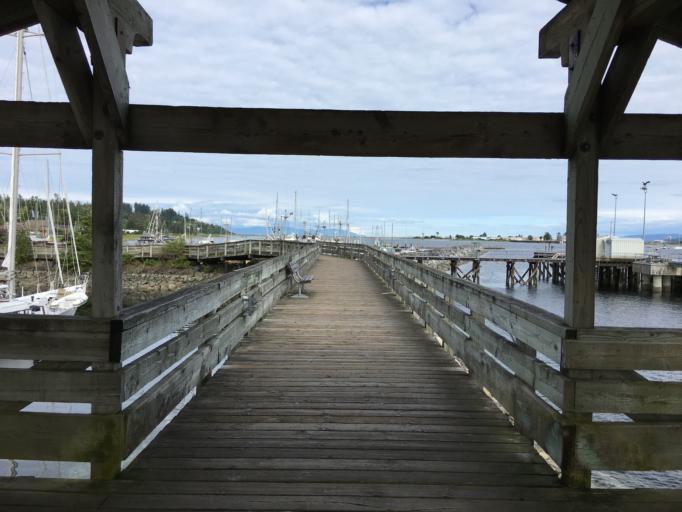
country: CA
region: British Columbia
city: Courtenay
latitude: 49.6692
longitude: -124.9283
